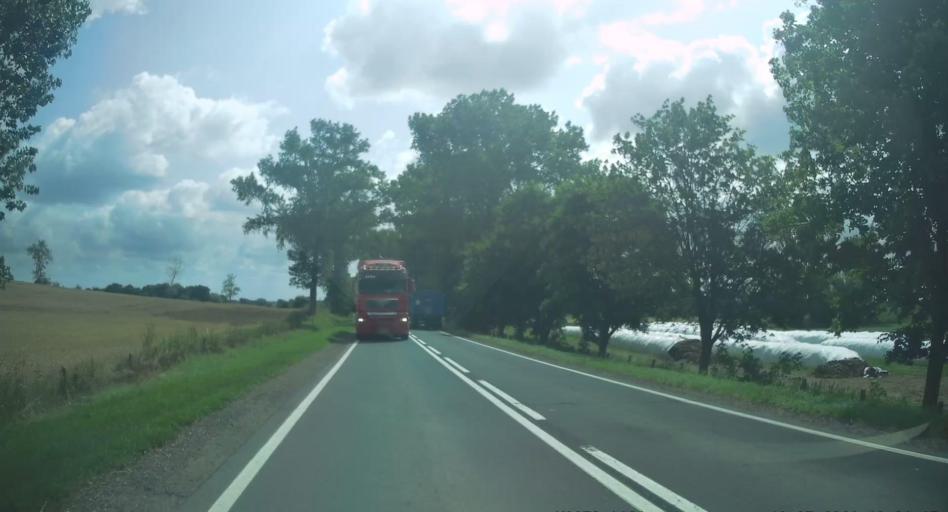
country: PL
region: Opole Voivodeship
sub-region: Powiat prudnicki
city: Twardawa
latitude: 50.3406
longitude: 17.9502
